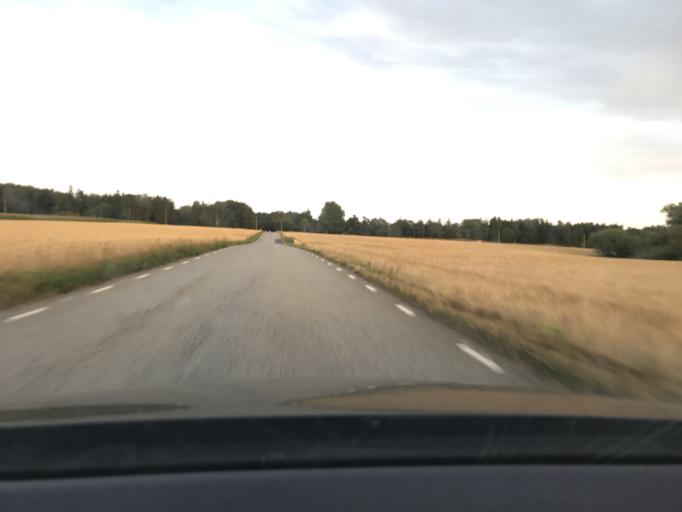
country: SE
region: Skane
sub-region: Simrishamns Kommun
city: Simrishamn
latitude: 55.4384
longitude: 14.2257
